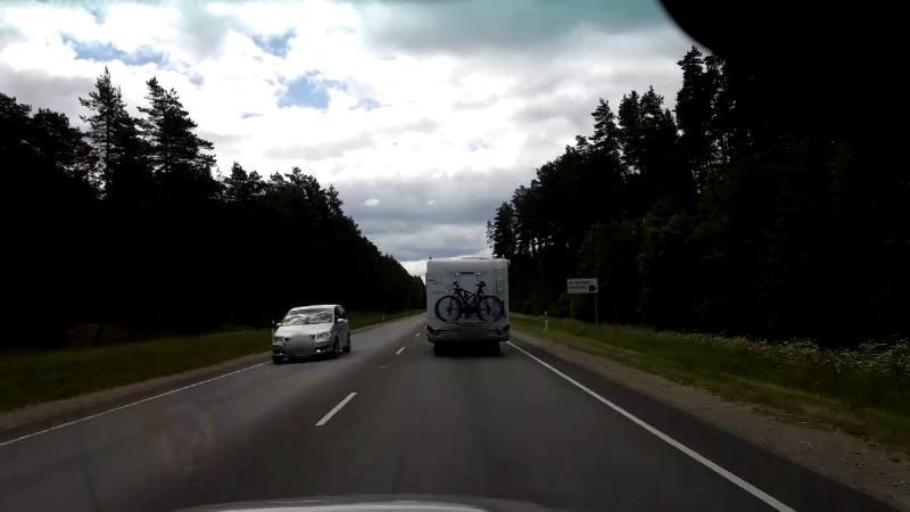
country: EE
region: Paernumaa
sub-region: Paikuse vald
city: Paikuse
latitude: 58.3353
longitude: 24.5928
